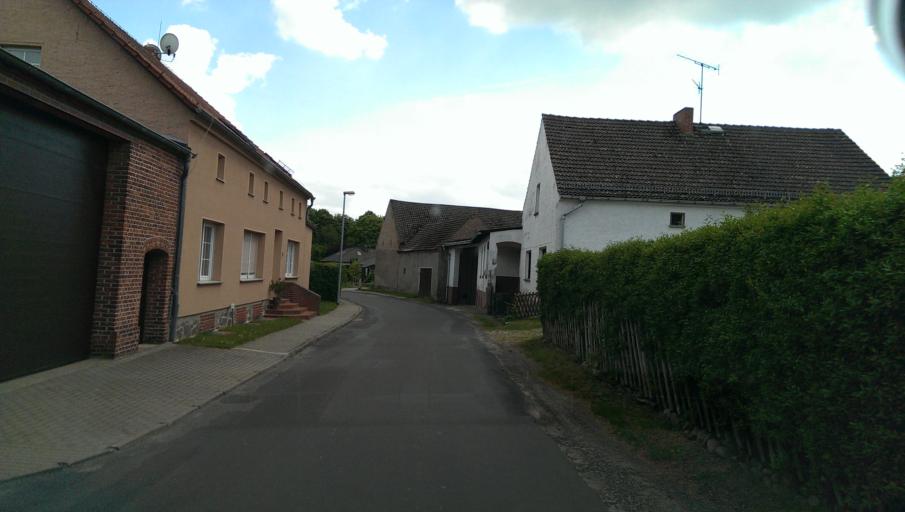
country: DE
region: Brandenburg
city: Wiesenburg
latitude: 52.1312
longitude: 12.5182
